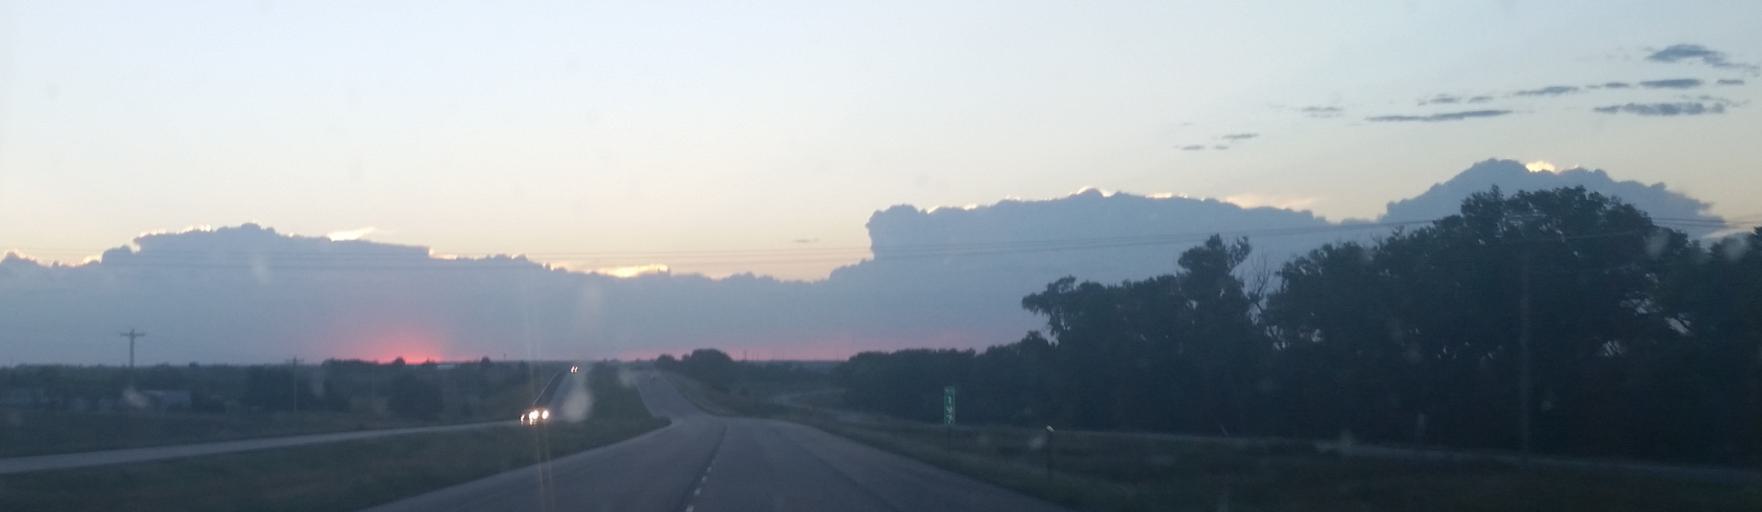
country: US
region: Kansas
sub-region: Russell County
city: Russell
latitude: 38.8567
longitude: -98.6342
